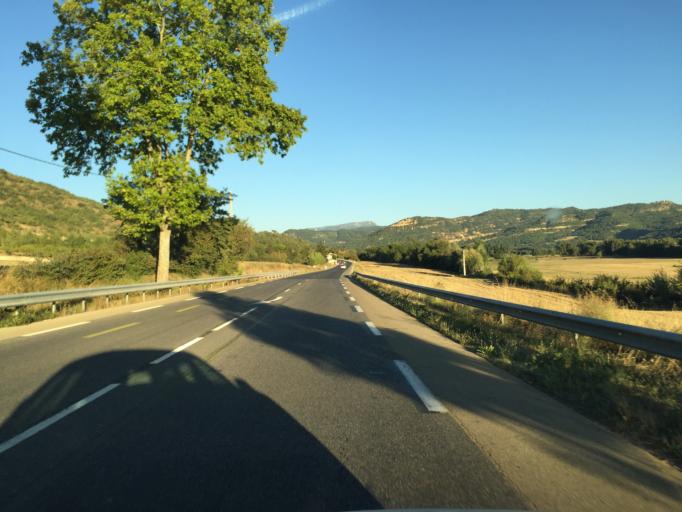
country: FR
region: Provence-Alpes-Cote d'Azur
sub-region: Departement des Alpes-de-Haute-Provence
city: Malijai
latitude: 44.0424
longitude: 6.0674
